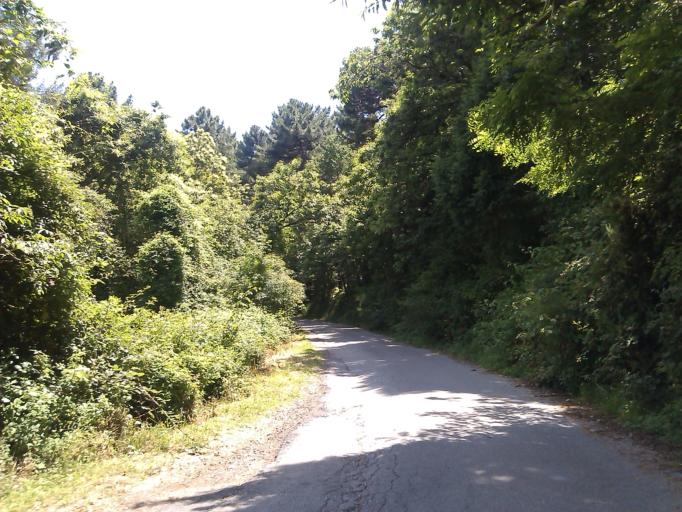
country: IT
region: Tuscany
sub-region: Provincia di Prato
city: Montemurlo
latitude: 43.9696
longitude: 11.0422
